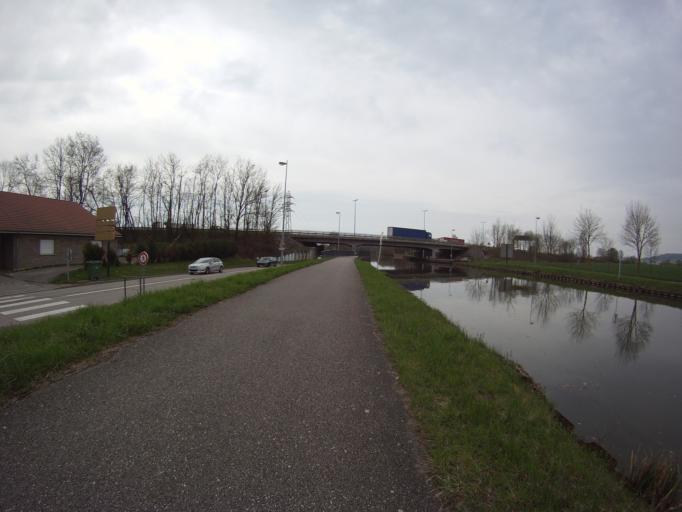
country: FR
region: Lorraine
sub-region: Departement de Meurthe-et-Moselle
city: Fleville-devant-Nancy
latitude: 48.6189
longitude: 6.2039
